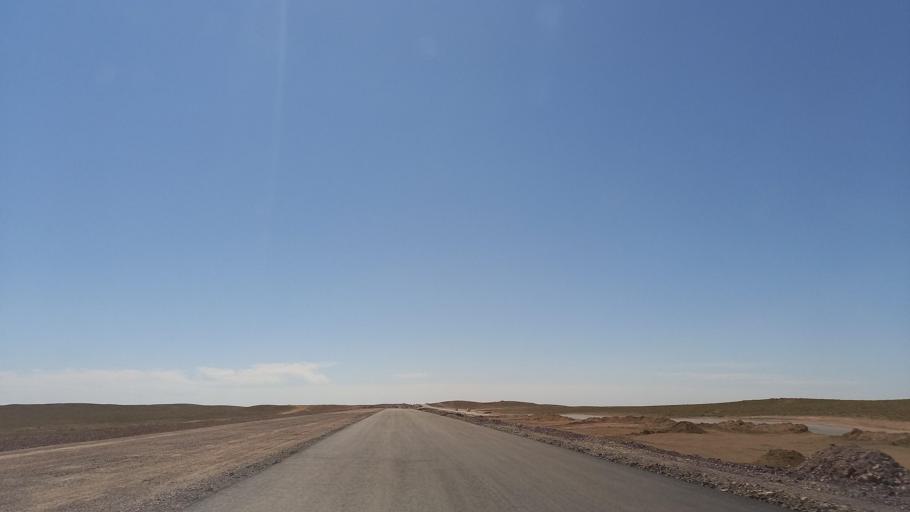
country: KZ
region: Zhambyl
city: Mynaral
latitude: 45.4887
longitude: 73.5321
